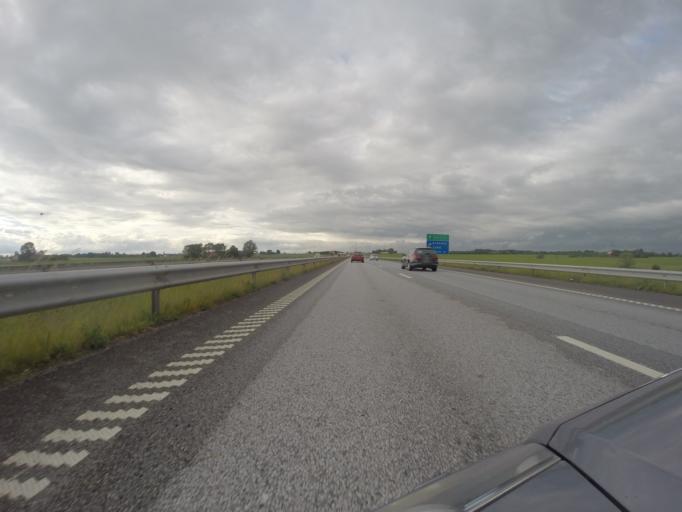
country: SE
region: Skane
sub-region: Lomma Kommun
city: Lomma
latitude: 55.7141
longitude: 13.0937
